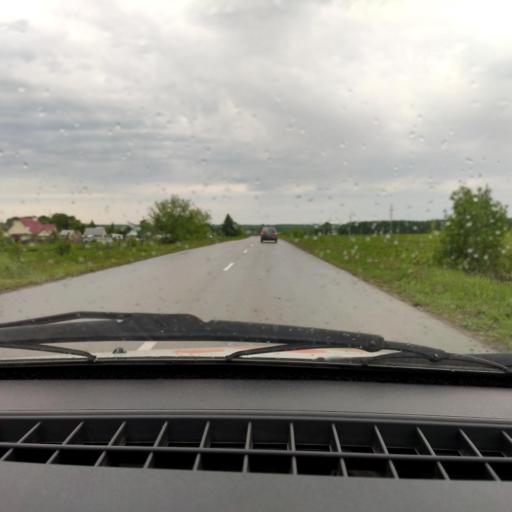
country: RU
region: Bashkortostan
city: Kudeyevskiy
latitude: 54.8453
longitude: 56.7958
